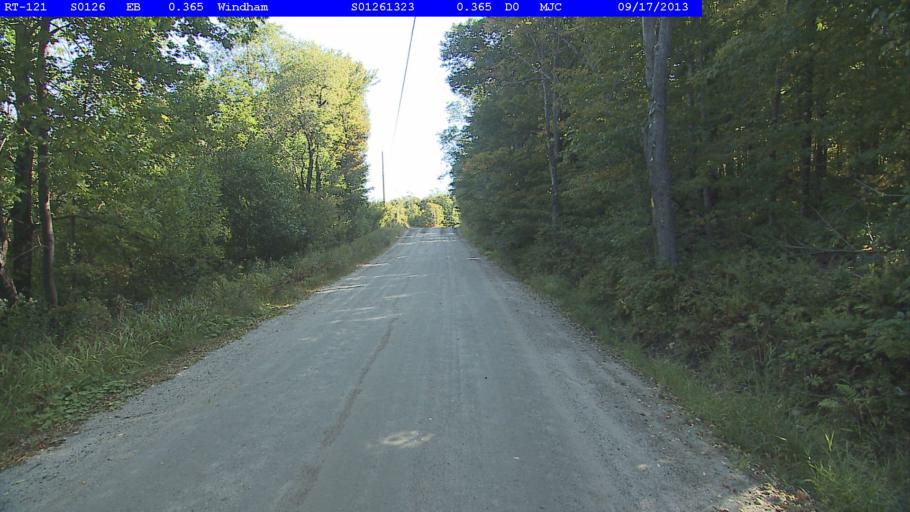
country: US
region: Vermont
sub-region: Windsor County
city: Chester
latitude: 43.1964
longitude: -72.7131
